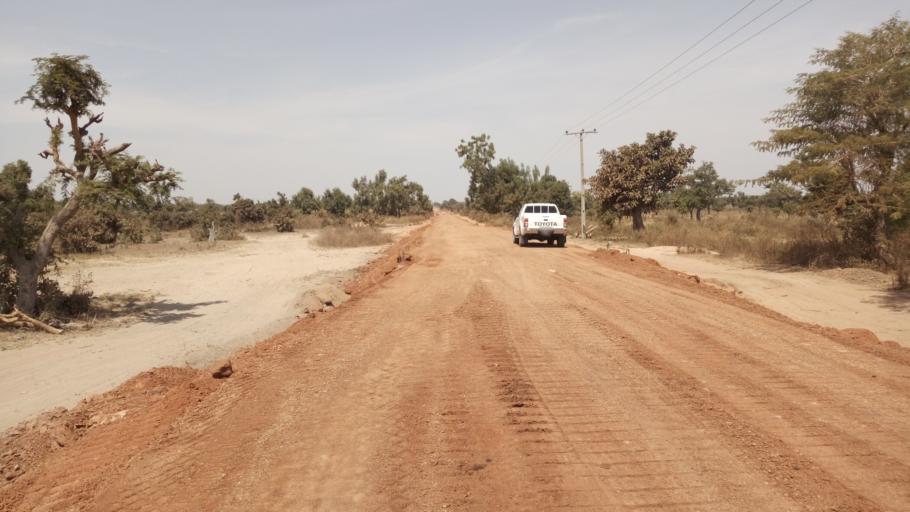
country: NG
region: Adamawa
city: Yola
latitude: 9.2267
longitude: 12.8784
